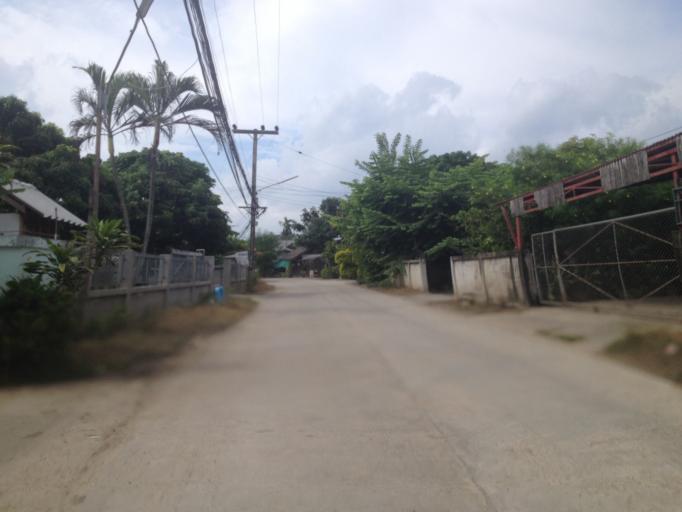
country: TH
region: Chiang Mai
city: Hang Dong
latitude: 18.6741
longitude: 98.9577
